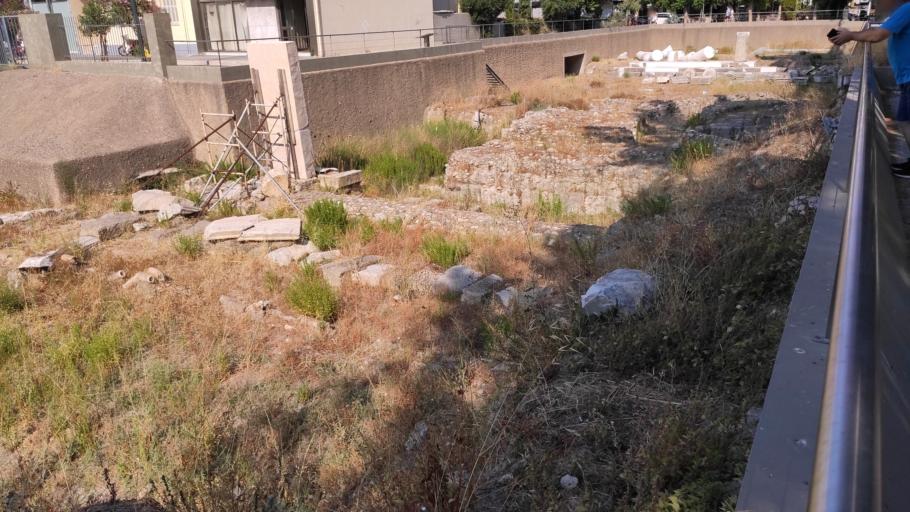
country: GR
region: South Aegean
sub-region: Nomos Dodekanisou
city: Kos
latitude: 36.8916
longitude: 27.2894
